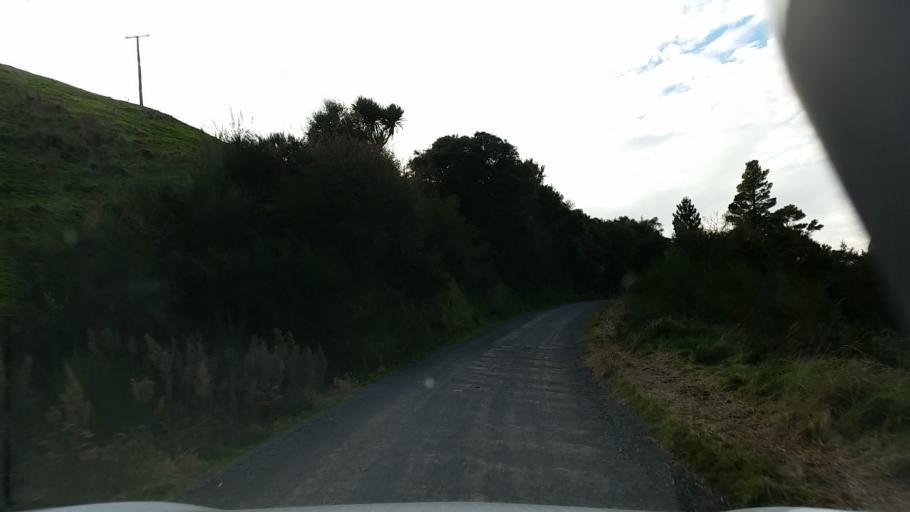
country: NZ
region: Bay of Plenty
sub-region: Rotorua District
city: Rotorua
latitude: -38.3014
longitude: 176.2670
